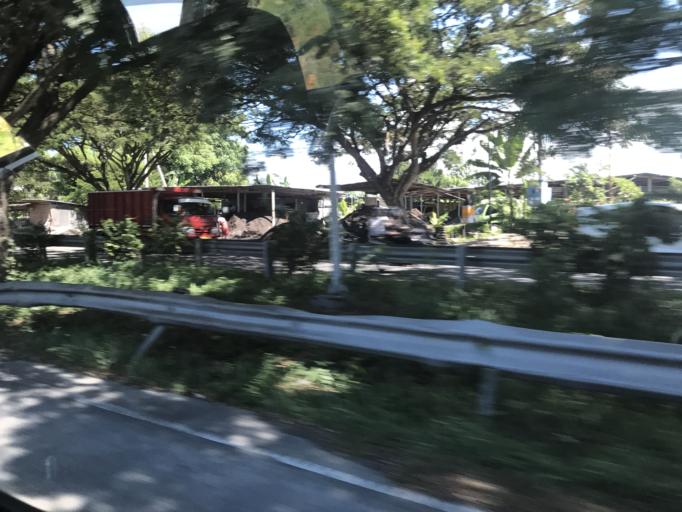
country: ID
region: Bali
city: Semarapura
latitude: -8.5653
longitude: 115.4166
